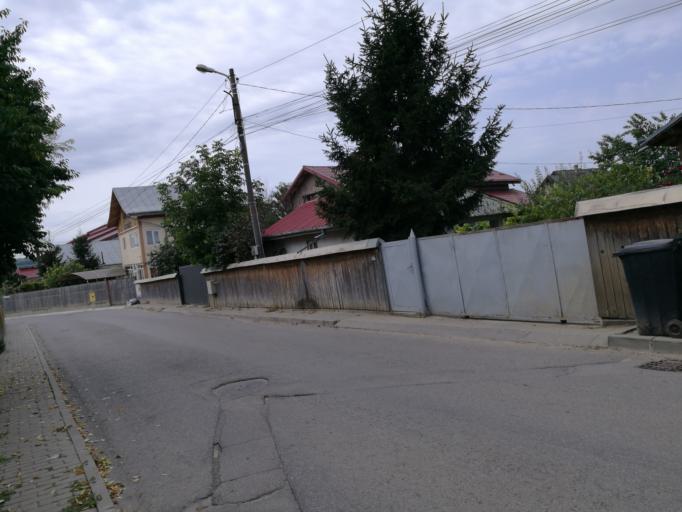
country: RO
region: Iasi
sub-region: Comuna Miroslava
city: Miroslava
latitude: 47.1747
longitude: 27.5285
